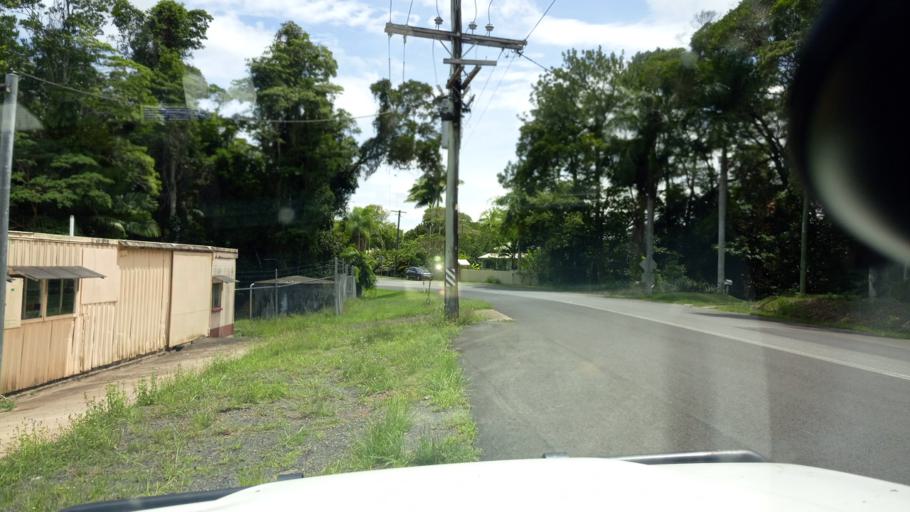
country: AU
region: Queensland
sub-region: Tablelands
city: Kuranda
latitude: -16.8155
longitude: 145.6209
